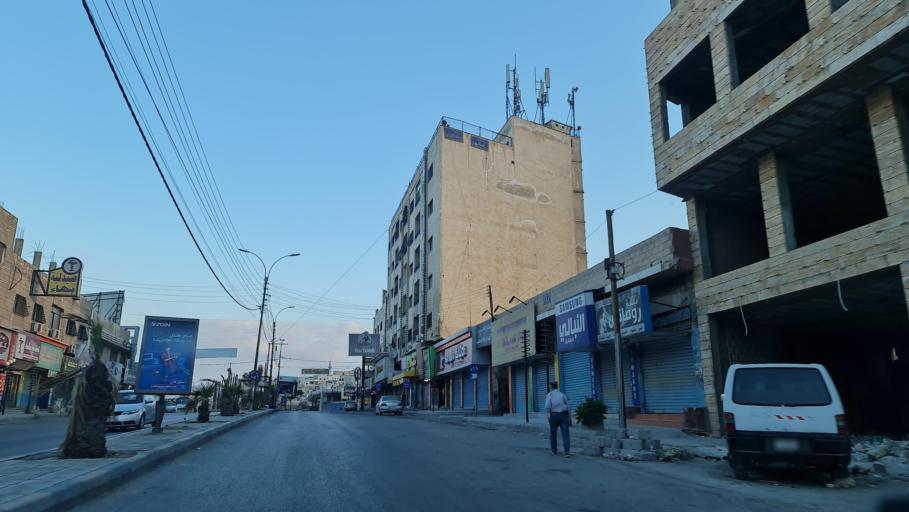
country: JO
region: Zarqa
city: Zarqa
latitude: 32.0775
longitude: 36.0757
